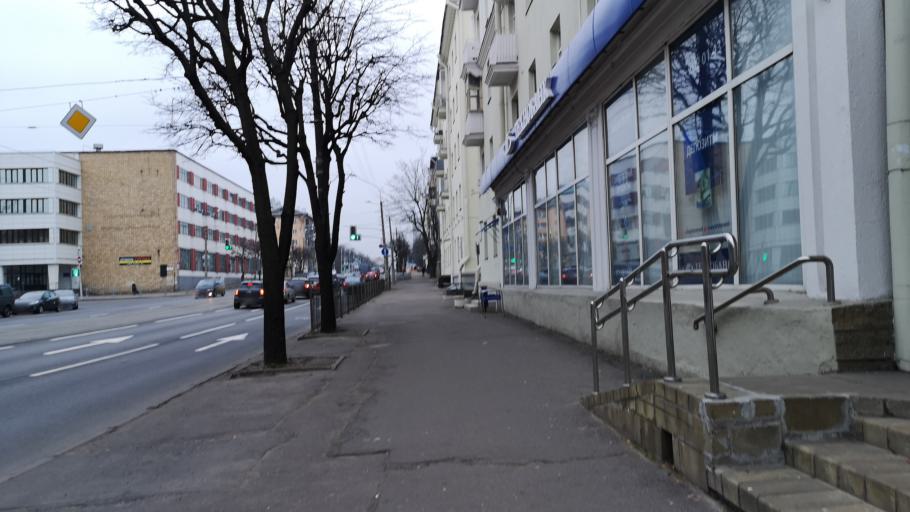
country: BY
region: Minsk
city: Minsk
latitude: 53.9182
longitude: 27.5856
